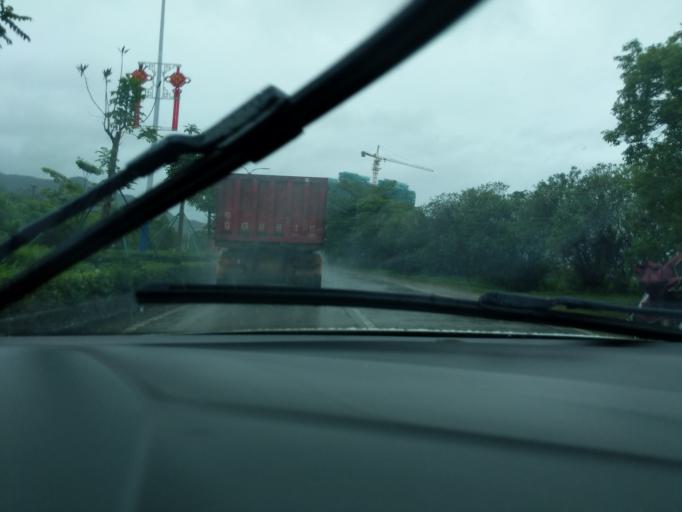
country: CN
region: Guangdong
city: Pingshi
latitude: 22.2105
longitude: 112.3243
